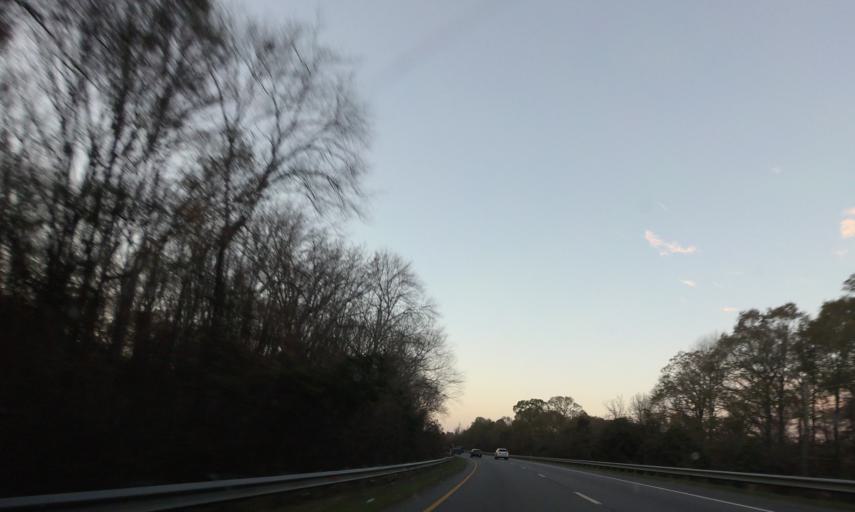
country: US
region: Georgia
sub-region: Houston County
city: Warner Robins
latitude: 32.6665
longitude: -83.6197
